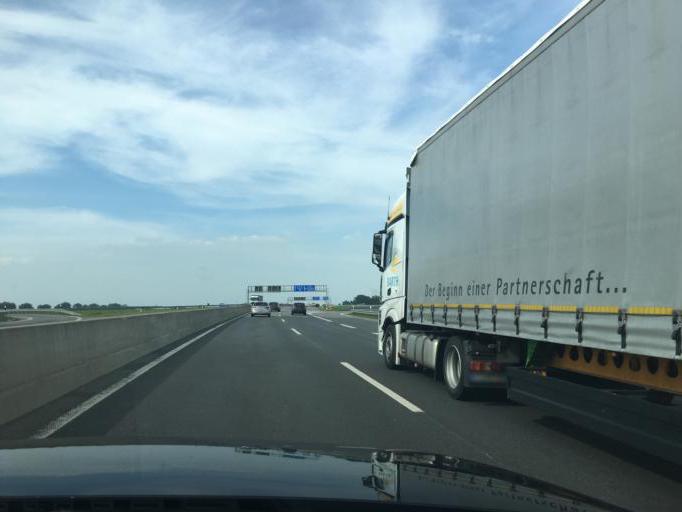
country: DE
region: North Rhine-Westphalia
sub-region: Regierungsbezirk Dusseldorf
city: Hochfeld
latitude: 51.3504
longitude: 6.7559
